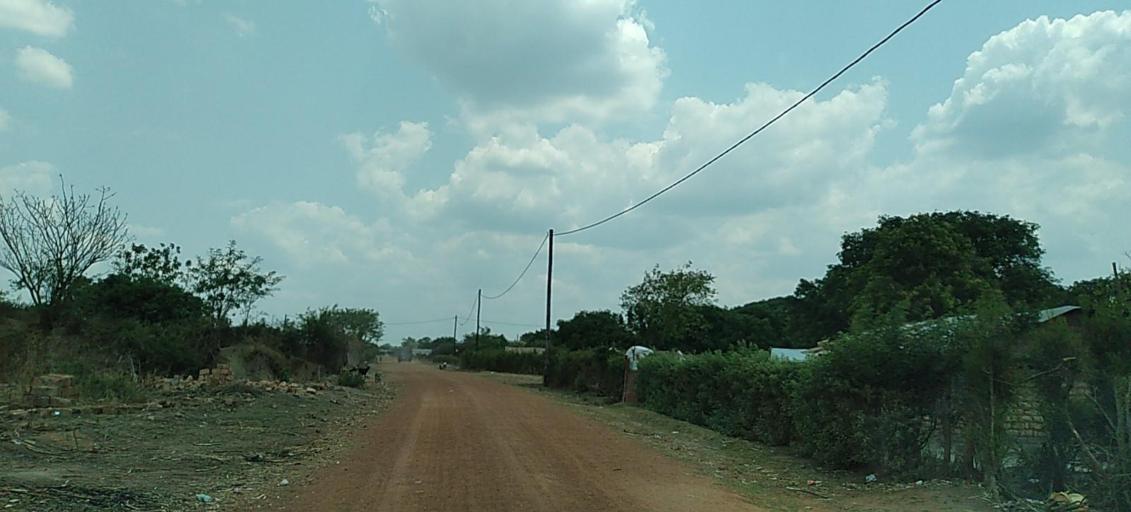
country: ZM
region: Copperbelt
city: Luanshya
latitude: -13.1236
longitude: 28.3103
